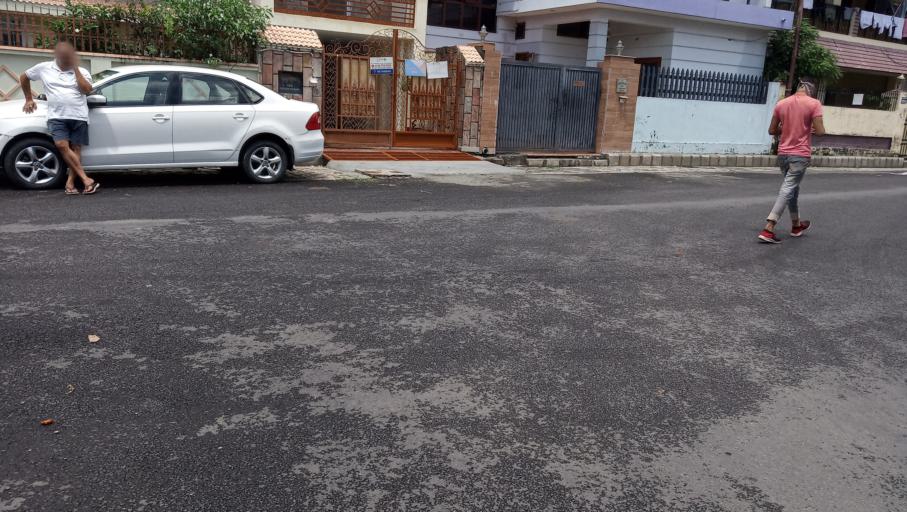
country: IN
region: Uttarakhand
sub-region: Dehradun
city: Dehradun
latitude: 30.3657
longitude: 78.0646
